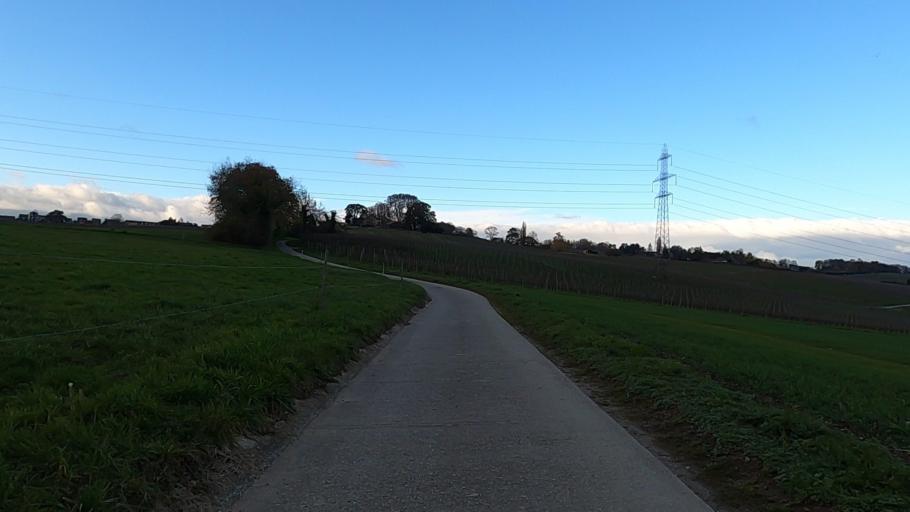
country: CH
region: Vaud
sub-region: Morges District
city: Saint-Prex
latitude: 46.5133
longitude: 6.4634
